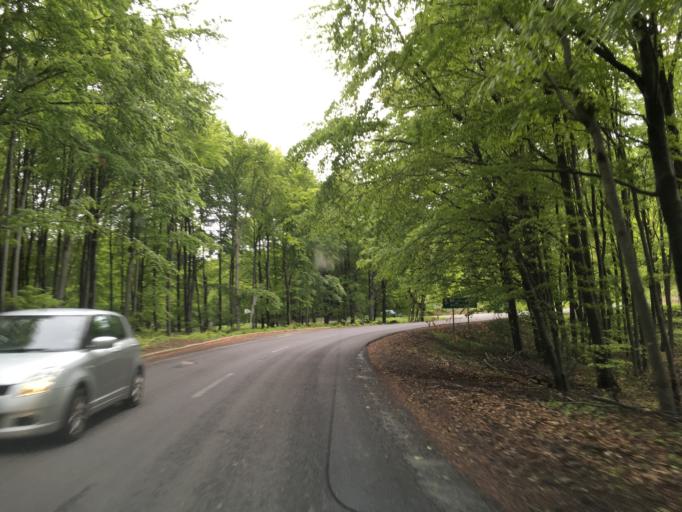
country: HU
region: Nograd
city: Batonyterenye
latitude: 47.9130
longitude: 19.8865
